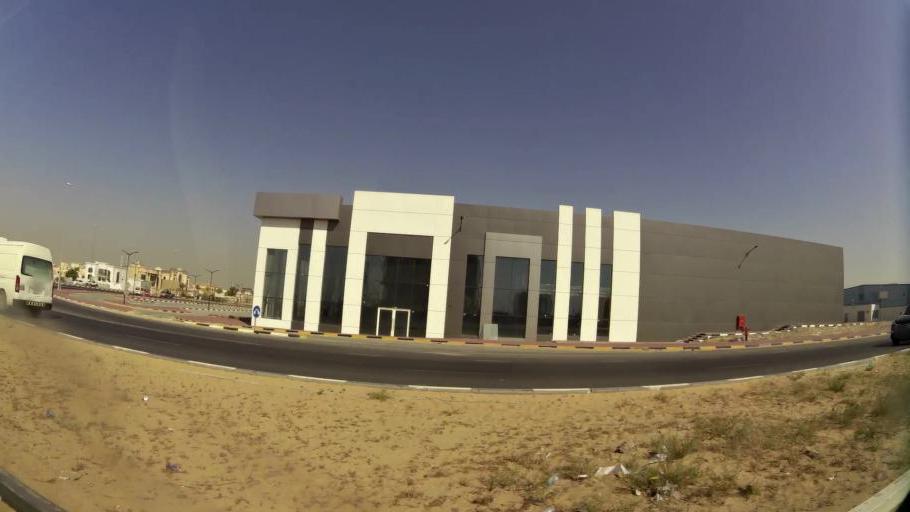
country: AE
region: Ajman
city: Ajman
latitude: 25.4234
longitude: 55.5312
